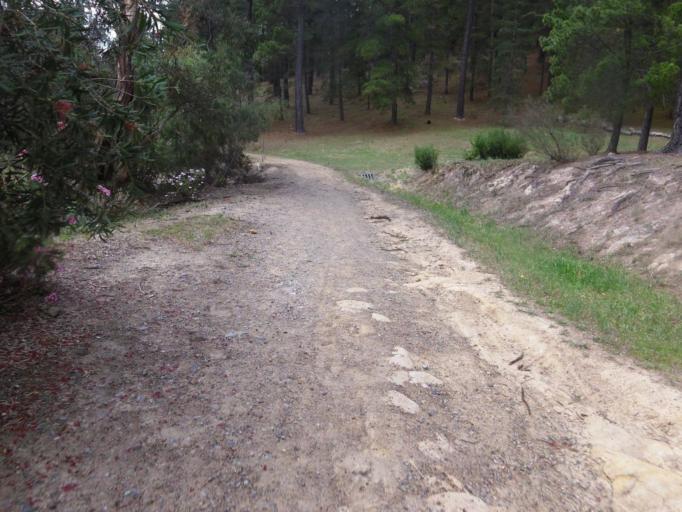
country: AU
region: Australian Capital Territory
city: Macarthur
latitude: -35.3747
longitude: 149.1186
